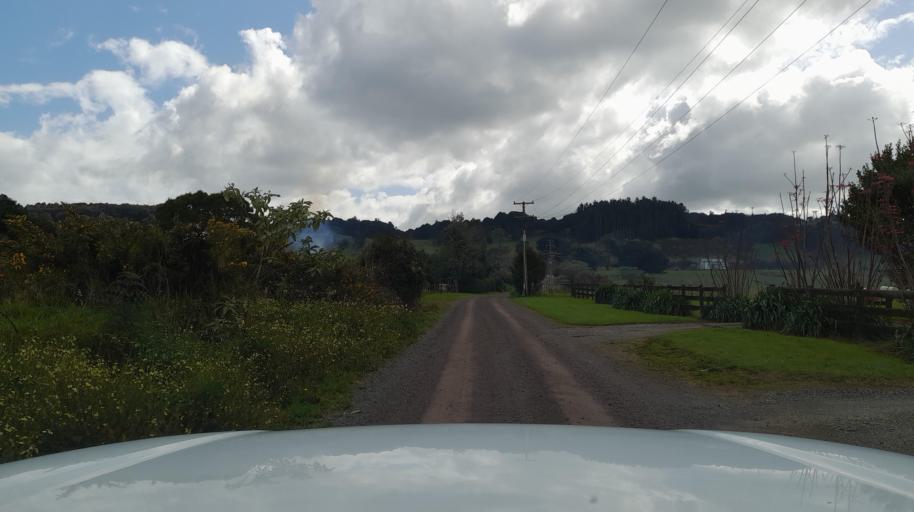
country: NZ
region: Northland
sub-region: Far North District
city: Waimate North
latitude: -35.3748
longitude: 173.8610
